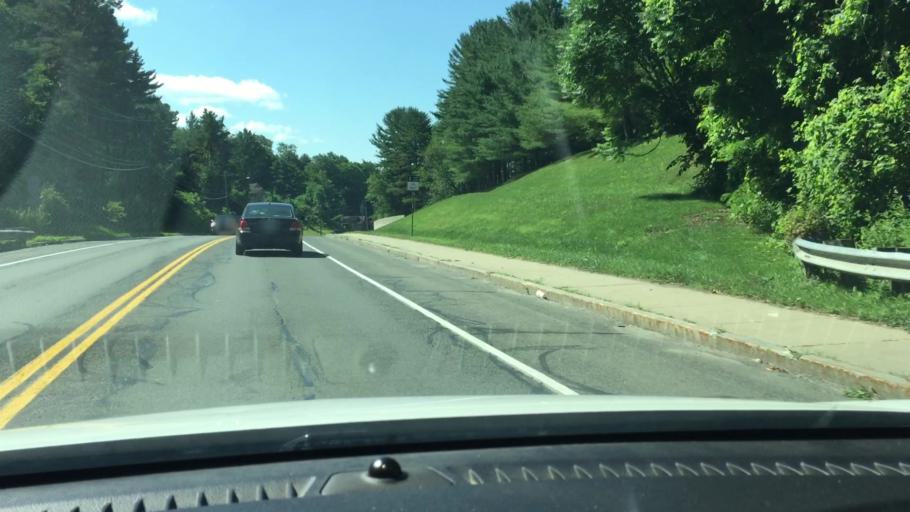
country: US
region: Massachusetts
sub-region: Berkshire County
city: Lanesborough
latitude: 42.4871
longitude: -73.2465
